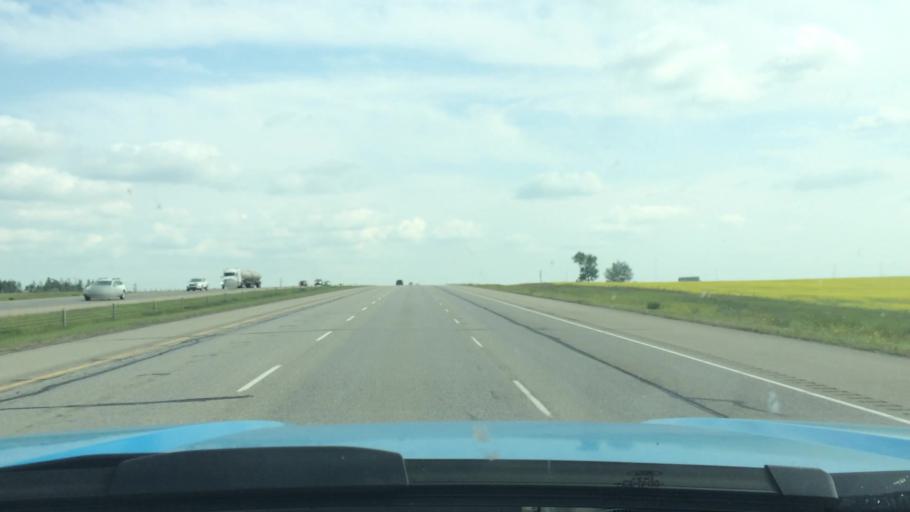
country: CA
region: Alberta
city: Crossfield
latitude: 51.4496
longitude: -114.0146
